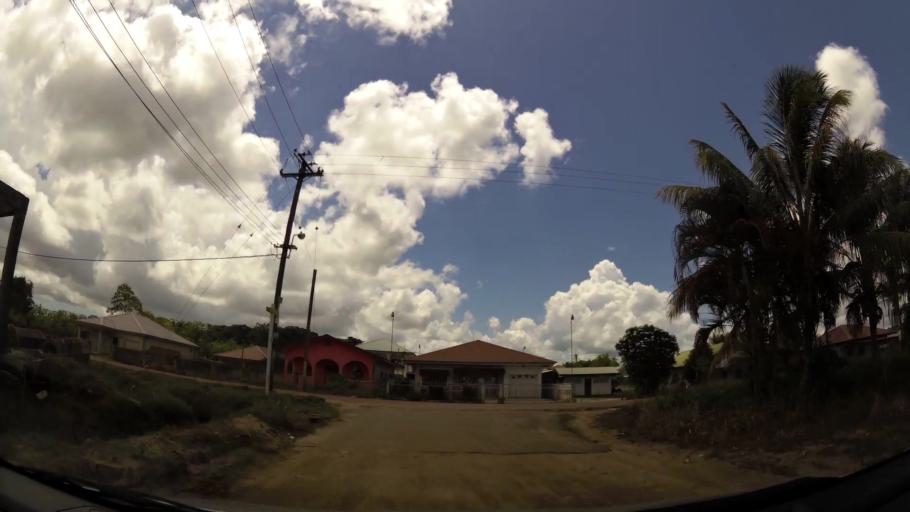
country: SR
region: Paramaribo
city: Paramaribo
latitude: 5.8636
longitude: -55.1666
